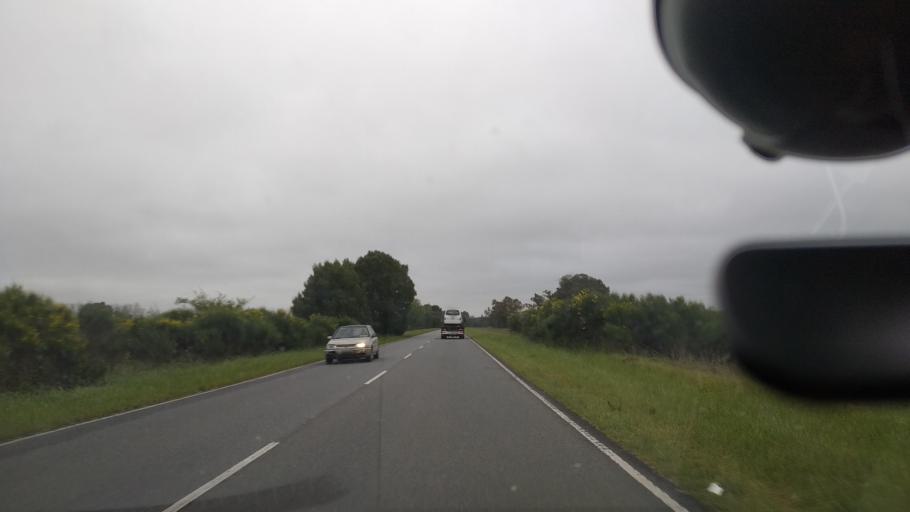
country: AR
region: Buenos Aires
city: Veronica
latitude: -35.4312
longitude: -57.3439
